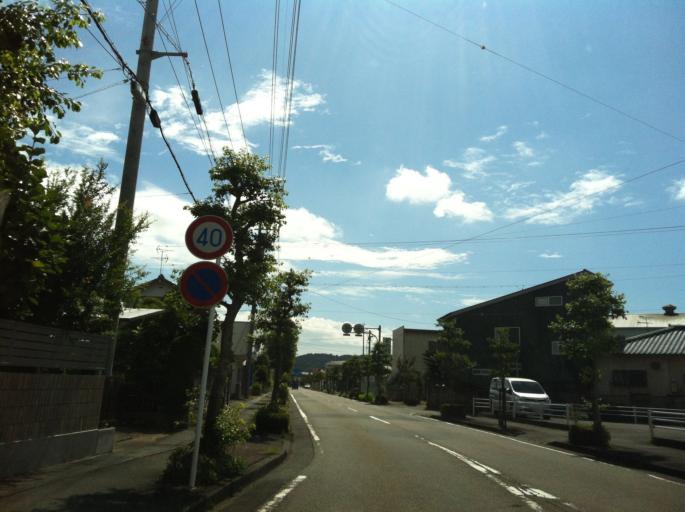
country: JP
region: Shizuoka
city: Kanaya
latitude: 34.8304
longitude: 138.1287
